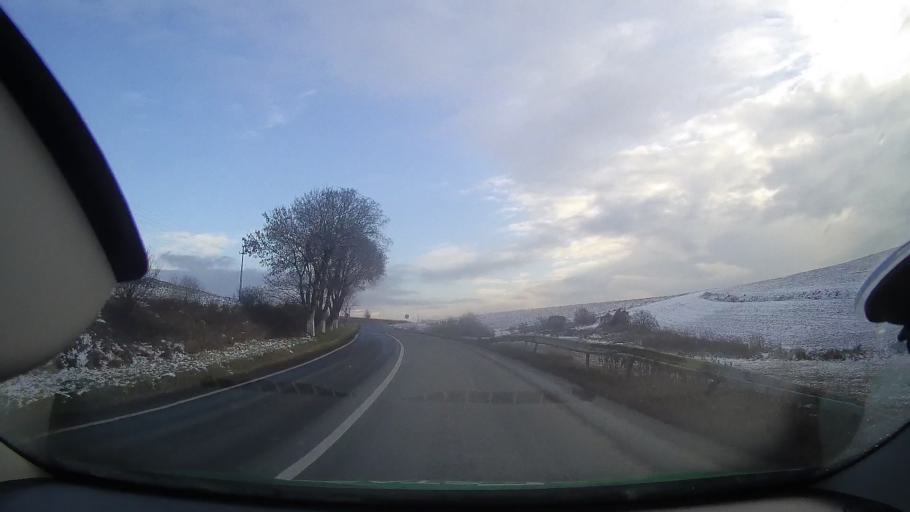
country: RO
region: Mures
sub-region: Comuna Cucerdea
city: Cucerdea
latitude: 46.4190
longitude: 24.2595
